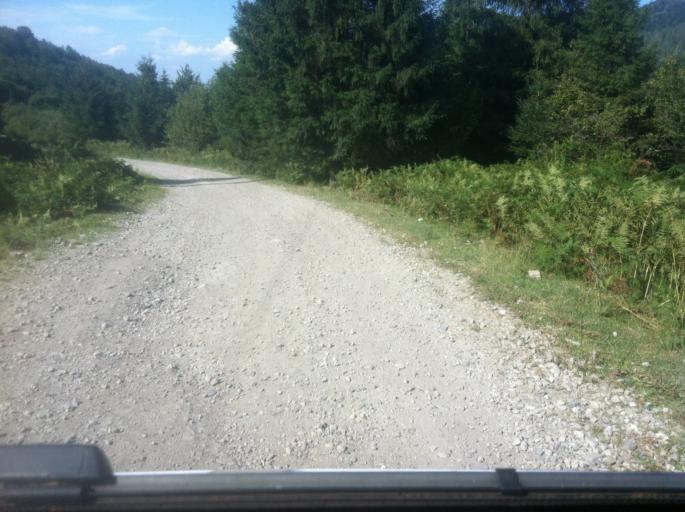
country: RO
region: Hunedoara
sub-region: Comuna Rau de Mori
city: Rau de Mori
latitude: 45.4428
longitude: 22.8940
